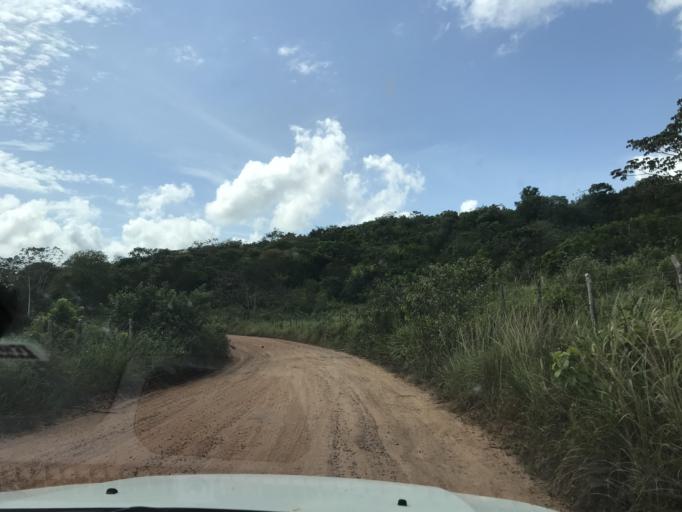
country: BR
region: Bahia
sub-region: Entre Rios
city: Entre Rios
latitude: -12.1778
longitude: -38.0621
